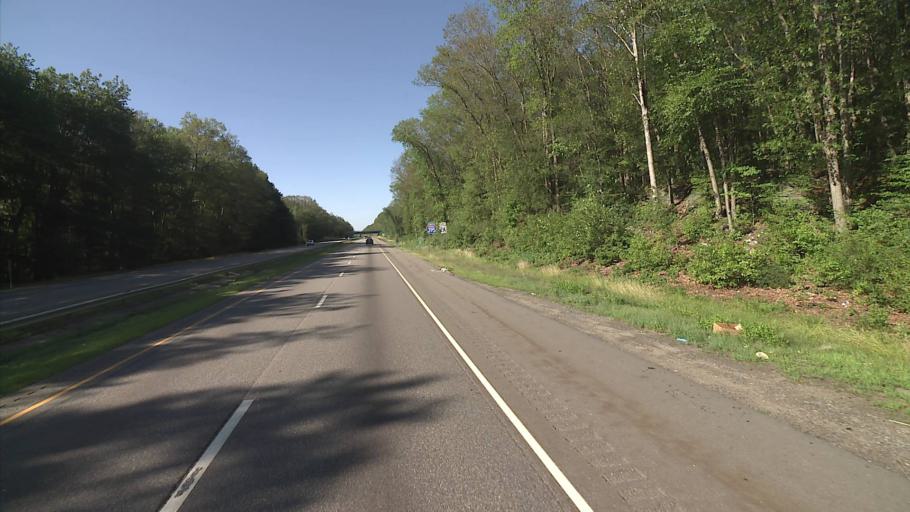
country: US
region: Connecticut
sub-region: New London County
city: Norwich
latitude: 41.5412
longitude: -72.1113
